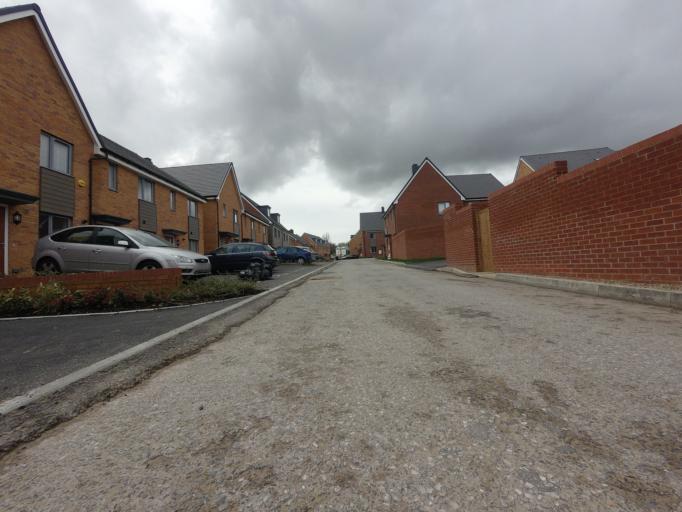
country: GB
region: England
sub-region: Kent
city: Swanley
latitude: 51.3918
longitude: 0.1778
